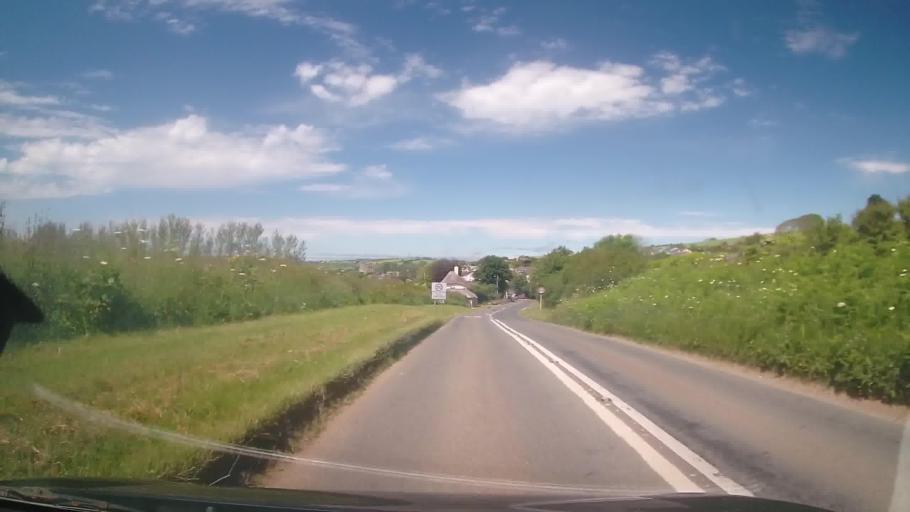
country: GB
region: England
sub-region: Devon
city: Kingsbridge
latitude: 50.2698
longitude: -3.7451
